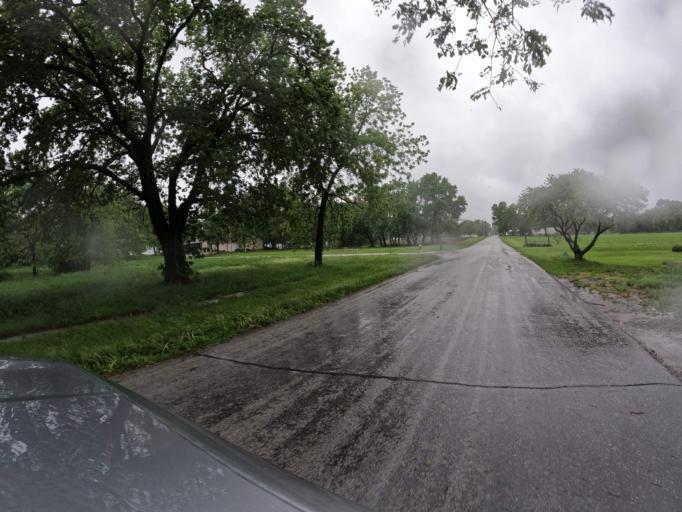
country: US
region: Nebraska
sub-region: Gage County
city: Wymore
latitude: 40.1355
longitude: -96.6598
